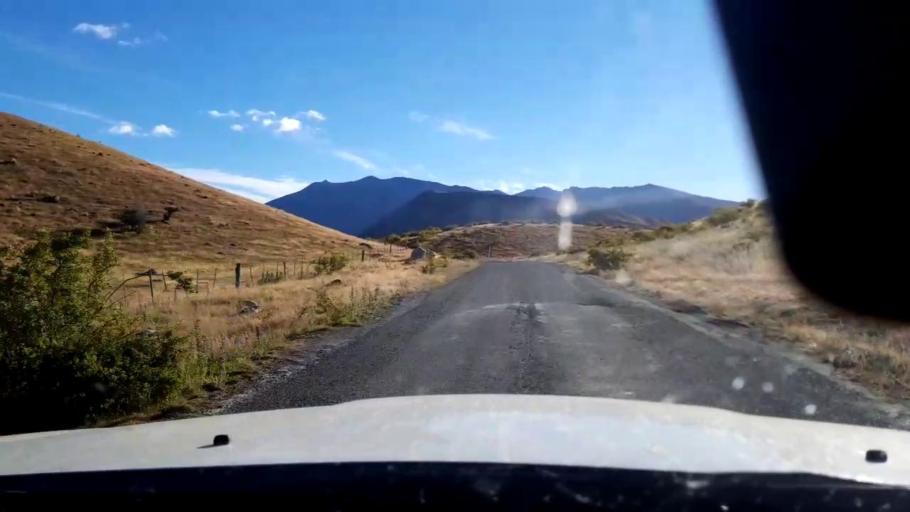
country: NZ
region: Canterbury
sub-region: Timaru District
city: Pleasant Point
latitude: -43.9657
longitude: 170.5208
